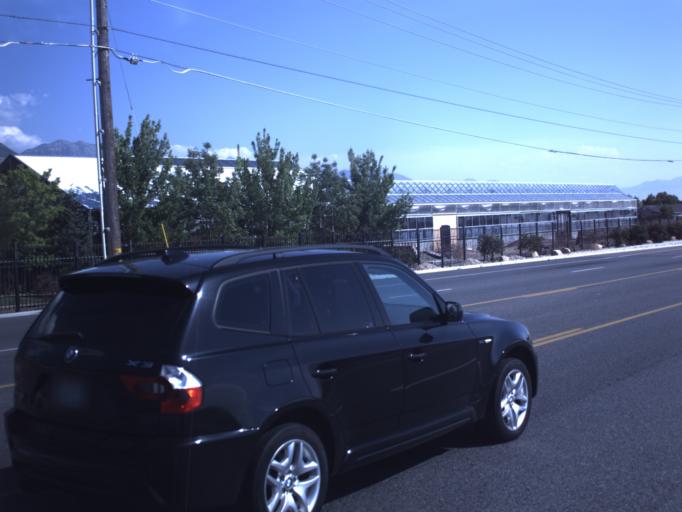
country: US
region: Utah
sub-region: Utah County
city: Cedar Hills
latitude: 40.4093
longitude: -111.7735
